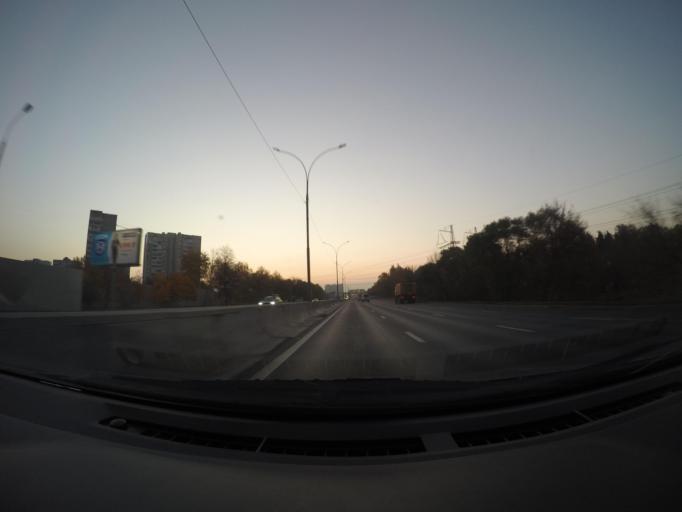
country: RU
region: Moscow
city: Vykhino-Zhulebino
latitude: 55.6924
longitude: 37.8174
